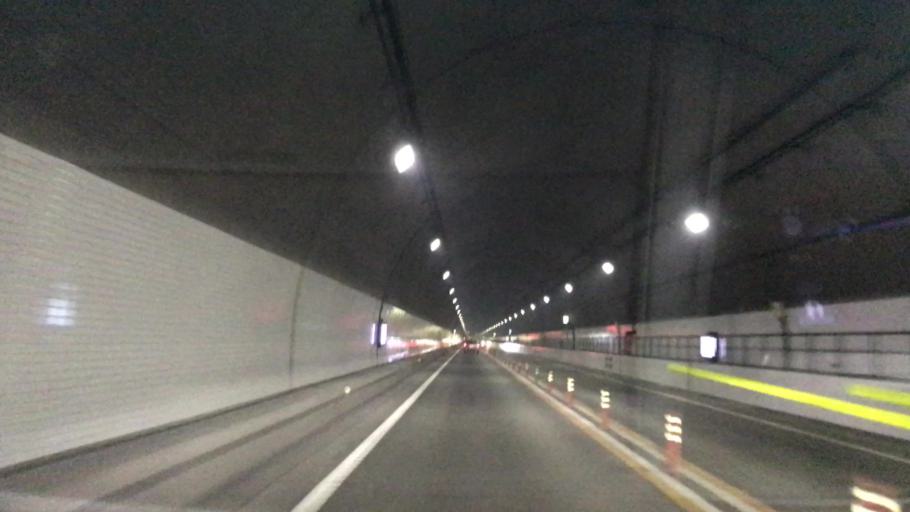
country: JP
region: Hokkaido
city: Shimo-furano
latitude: 42.9539
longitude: 142.3153
